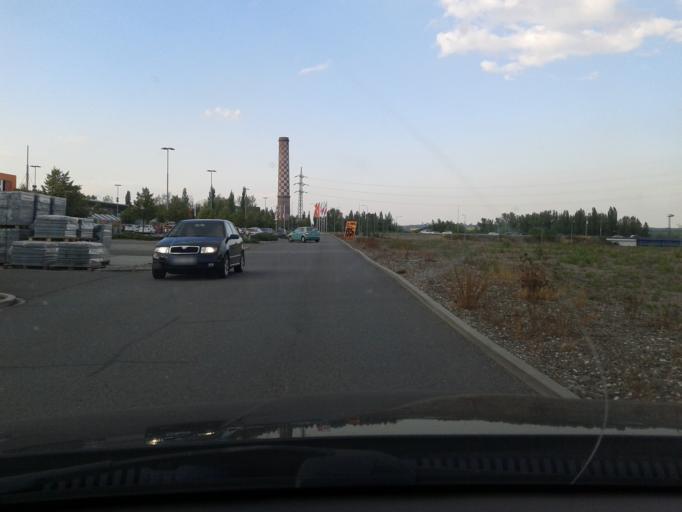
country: CZ
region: Moravskoslezsky
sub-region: Okres Ostrava-Mesto
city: Ostrava
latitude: 49.8041
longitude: 18.2786
